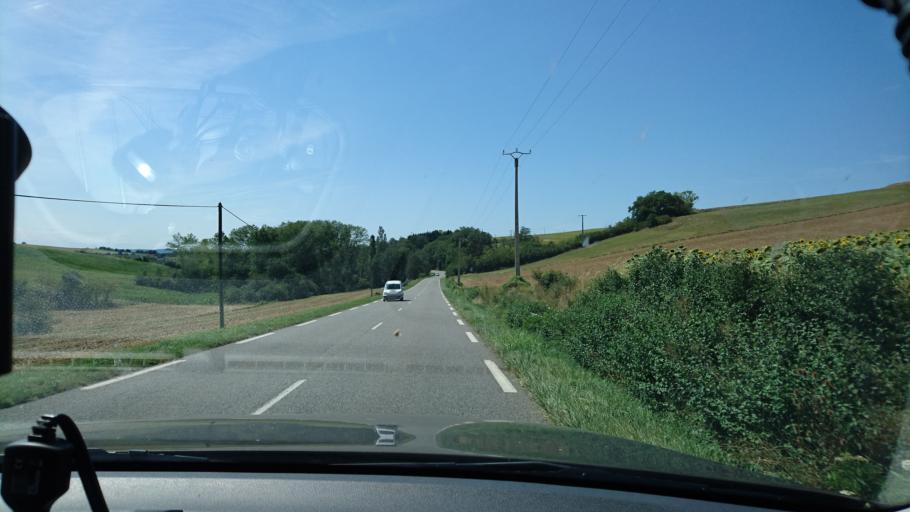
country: FR
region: Midi-Pyrenees
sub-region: Departement de la Haute-Garonne
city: Noe
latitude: 43.3391
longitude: 1.2887
